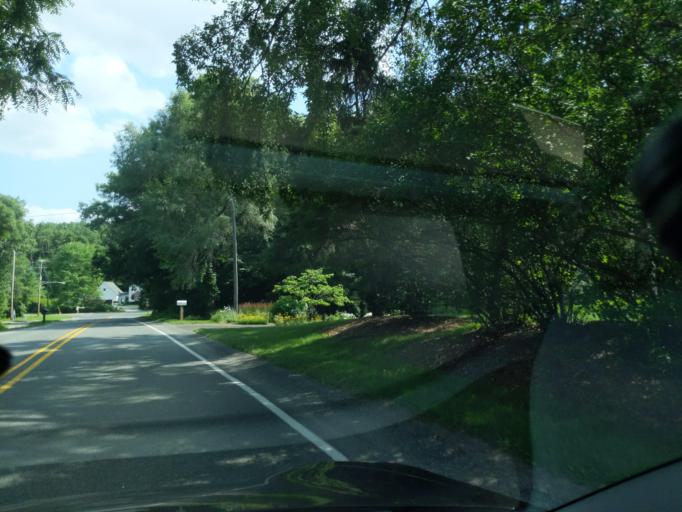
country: US
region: Michigan
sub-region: Kent County
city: Forest Hills
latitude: 42.9674
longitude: -85.5312
